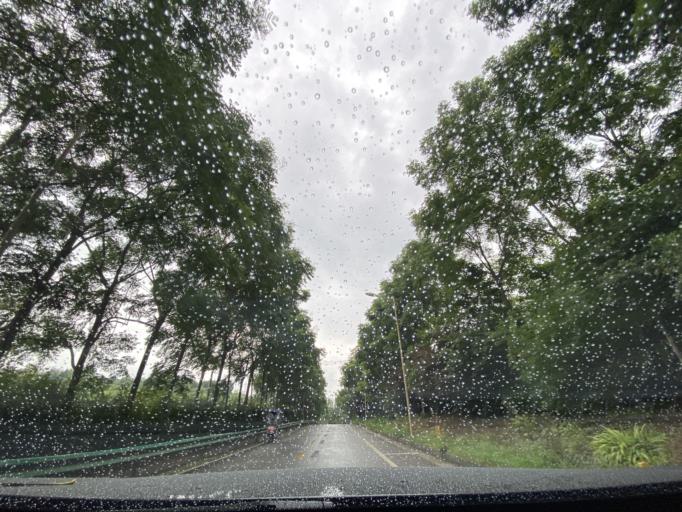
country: CN
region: Sichuan
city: Longquan
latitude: 30.6074
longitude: 104.4799
